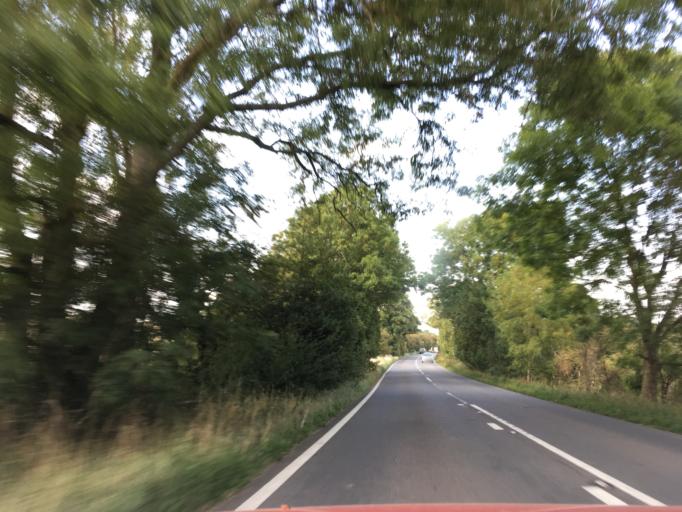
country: GB
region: England
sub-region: Gloucestershire
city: Bourton on the Water
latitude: 51.8633
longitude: -1.7985
